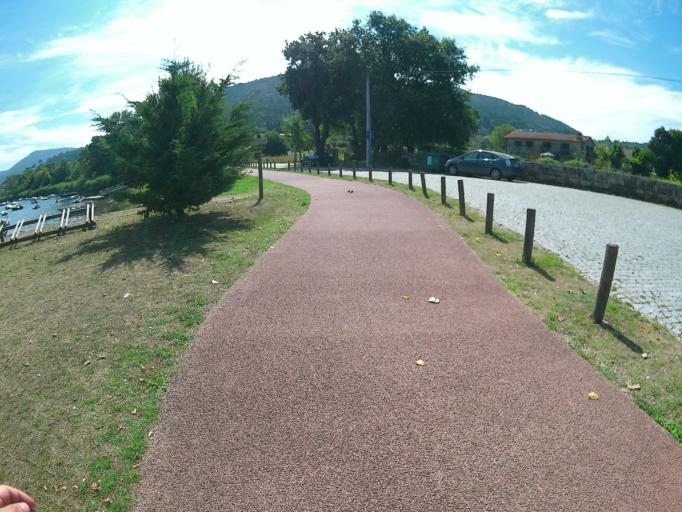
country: ES
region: Galicia
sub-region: Provincia de Pontevedra
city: O Rosal
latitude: 41.9143
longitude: -8.7893
